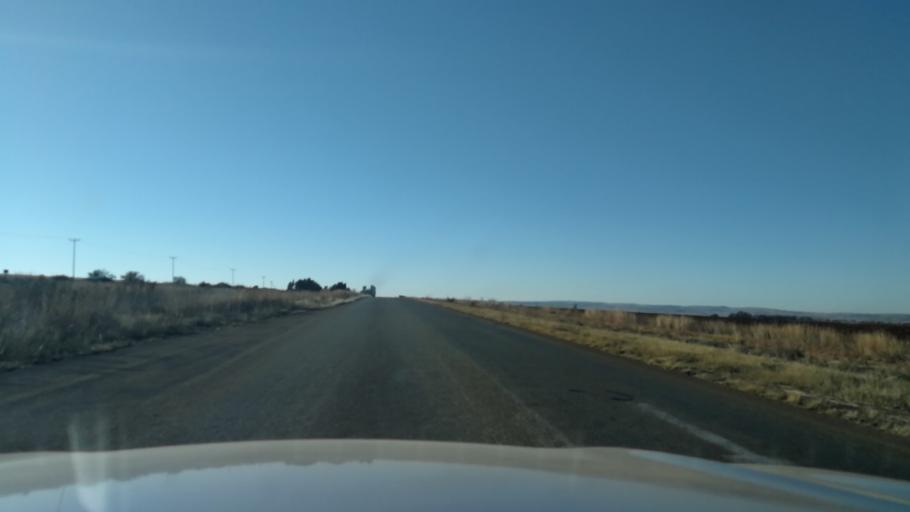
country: ZA
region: North-West
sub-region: Bojanala Platinum District Municipality
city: Rustenburg
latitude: -25.9655
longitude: 27.2167
